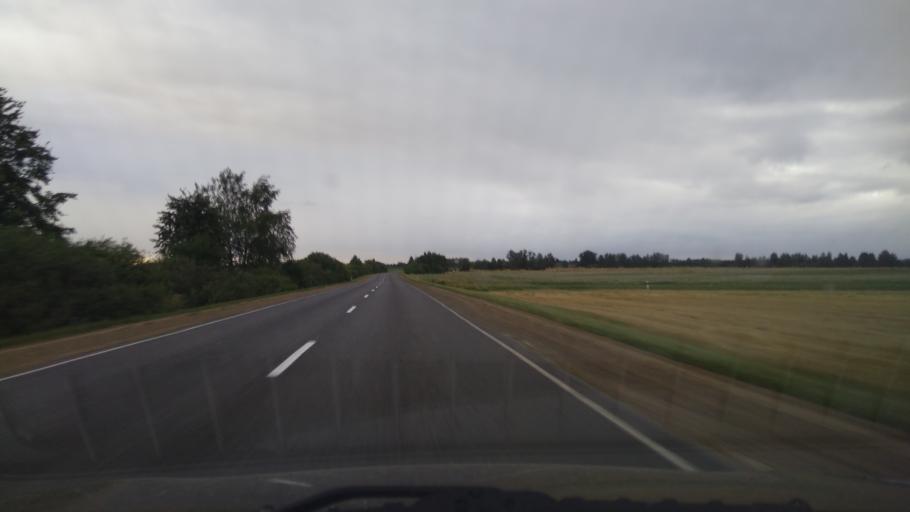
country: BY
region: Brest
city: Byaroza
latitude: 52.4435
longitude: 24.9744
